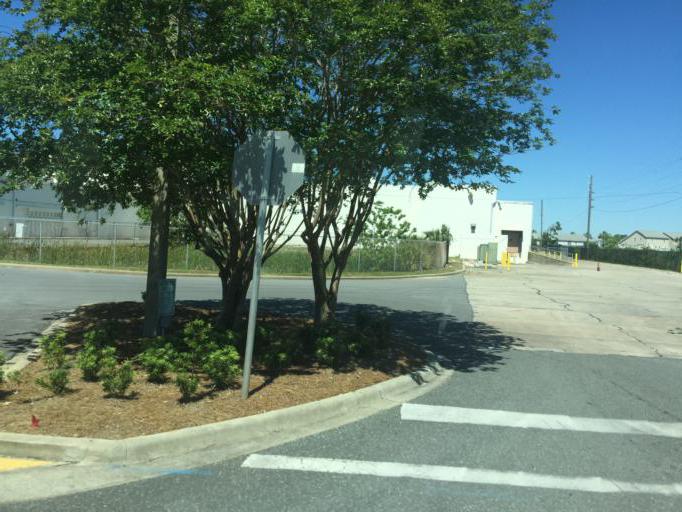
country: US
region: Florida
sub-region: Bay County
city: Panama City Beach
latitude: 30.1900
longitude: -85.8157
